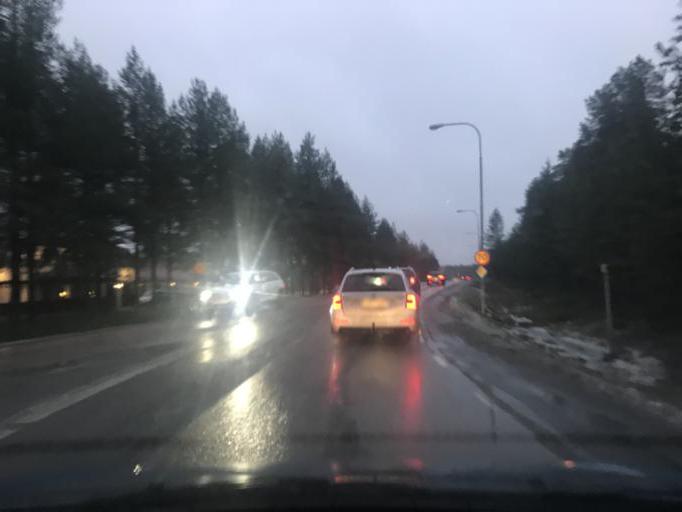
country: SE
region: Norrbotten
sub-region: Lulea Kommun
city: Gammelstad
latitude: 65.6250
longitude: 22.0360
